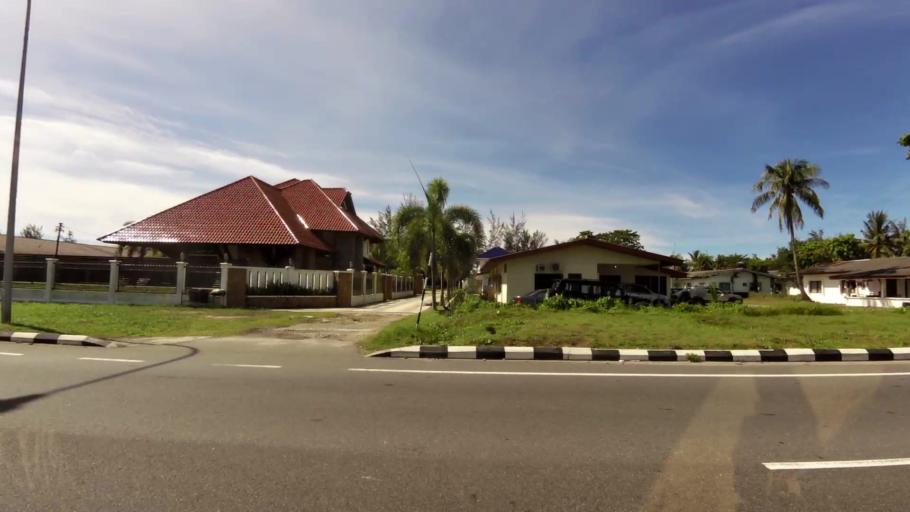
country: BN
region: Belait
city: Kuala Belait
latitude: 4.5894
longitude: 114.2086
